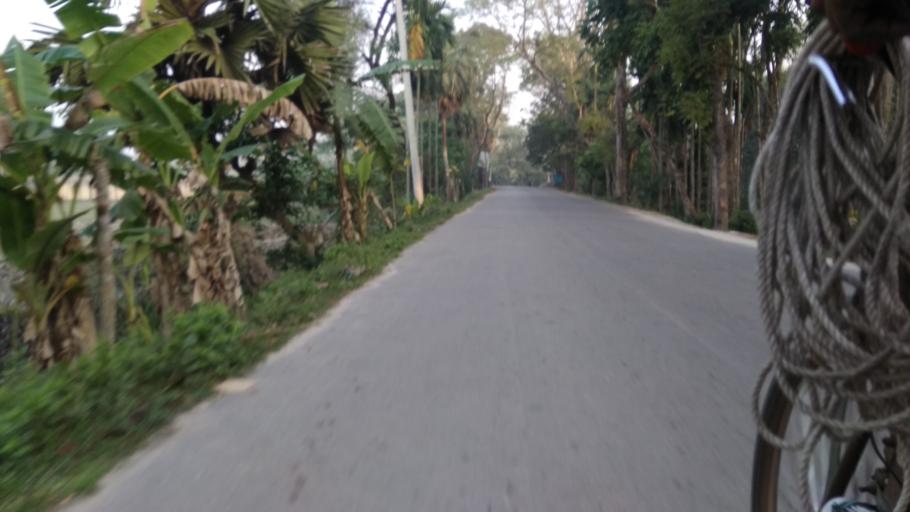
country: BD
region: Barisal
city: Mehendiganj
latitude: 22.9197
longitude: 90.4093
